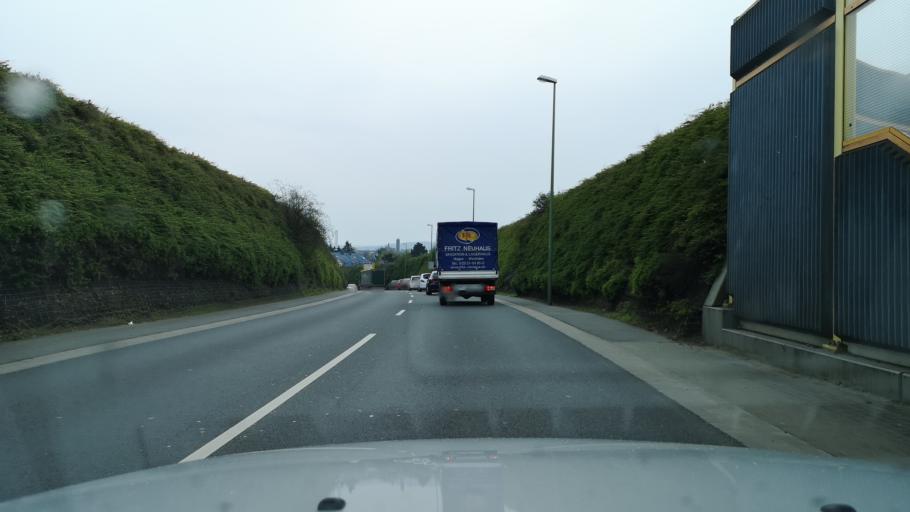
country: DE
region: North Rhine-Westphalia
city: Herdecke
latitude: 51.3940
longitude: 7.4653
